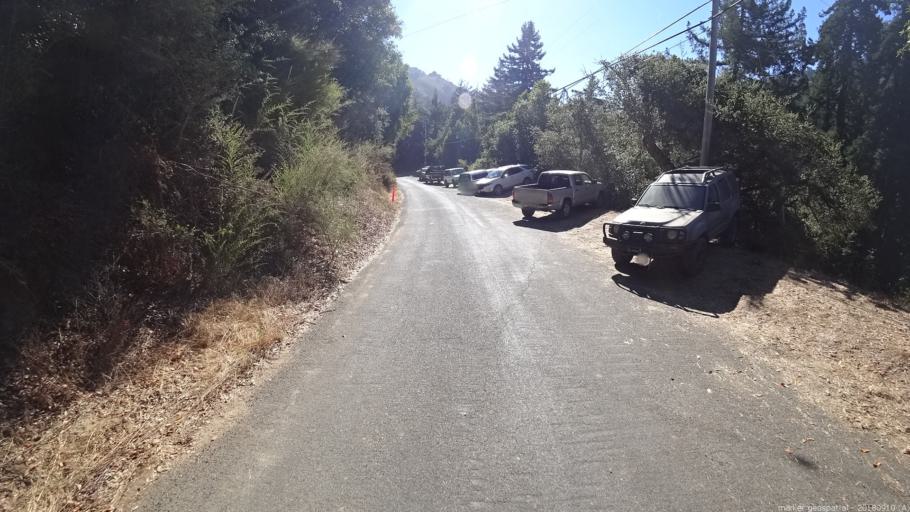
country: US
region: California
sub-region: Monterey County
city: Carmel Valley Village
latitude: 36.3842
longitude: -121.8676
